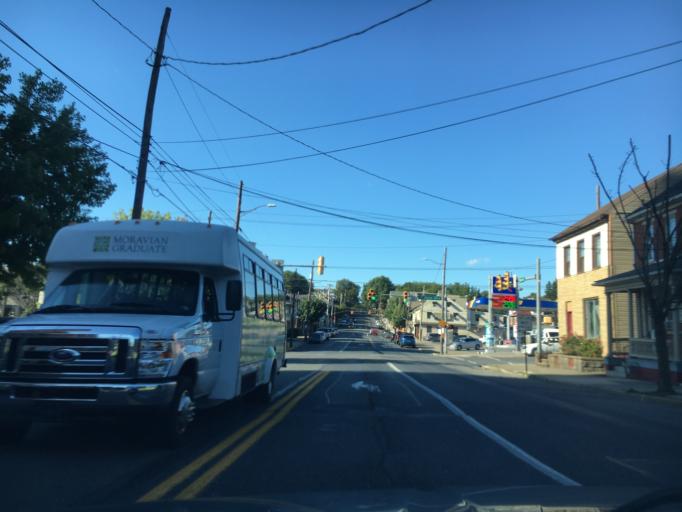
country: US
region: Pennsylvania
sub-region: Northampton County
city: Bethlehem
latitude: 40.6246
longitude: -75.3818
